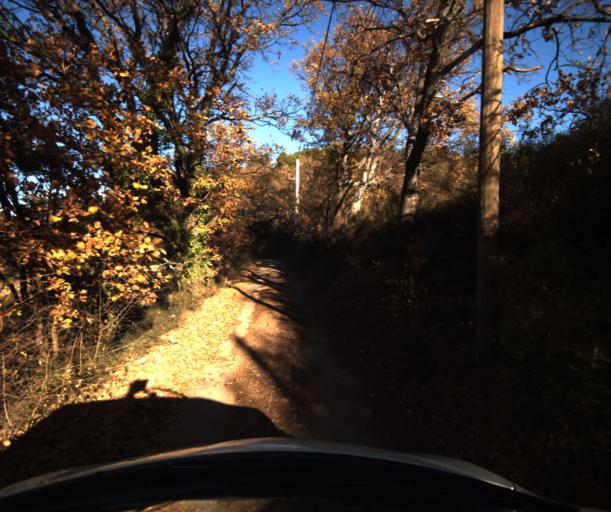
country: FR
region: Provence-Alpes-Cote d'Azur
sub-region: Departement du Vaucluse
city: Pertuis
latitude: 43.7143
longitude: 5.4978
